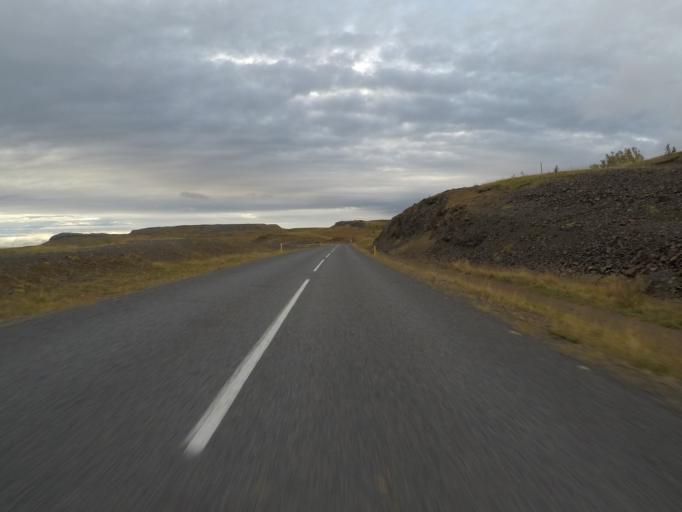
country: IS
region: South
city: Vestmannaeyjar
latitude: 64.0639
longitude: -20.0957
